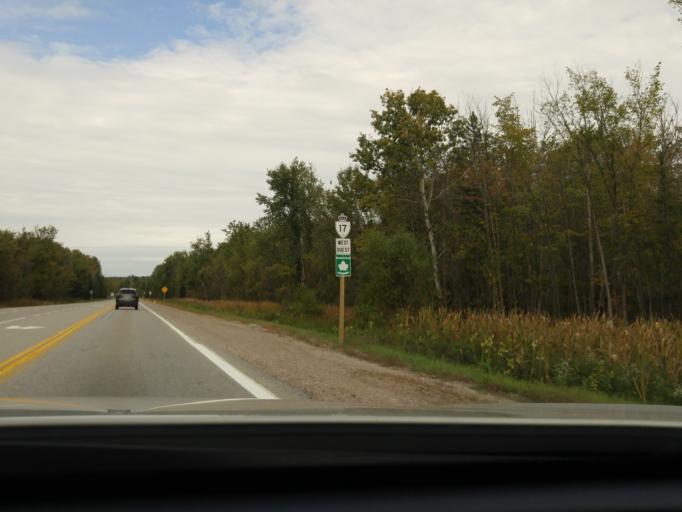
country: CA
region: Ontario
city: Renfrew
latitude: 45.5319
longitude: -76.6987
